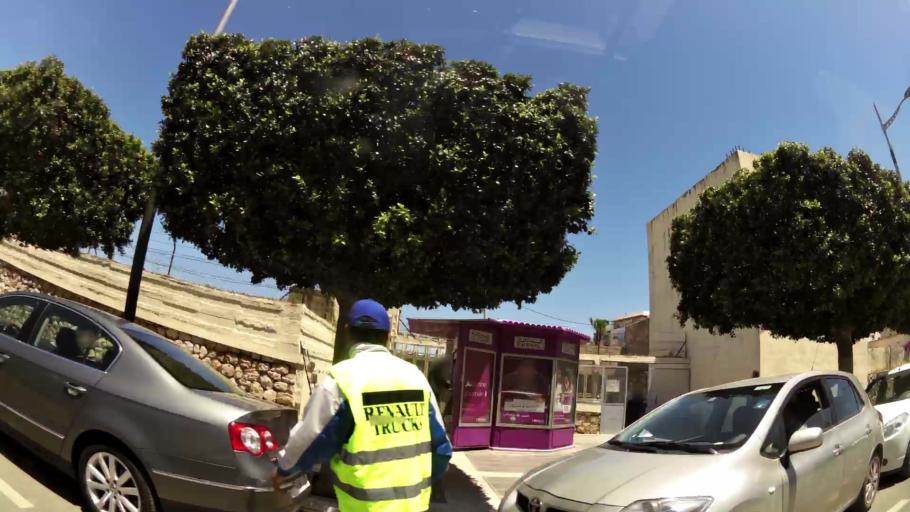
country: MA
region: Meknes-Tafilalet
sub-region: Meknes
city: Meknes
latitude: 33.9010
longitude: -5.5501
